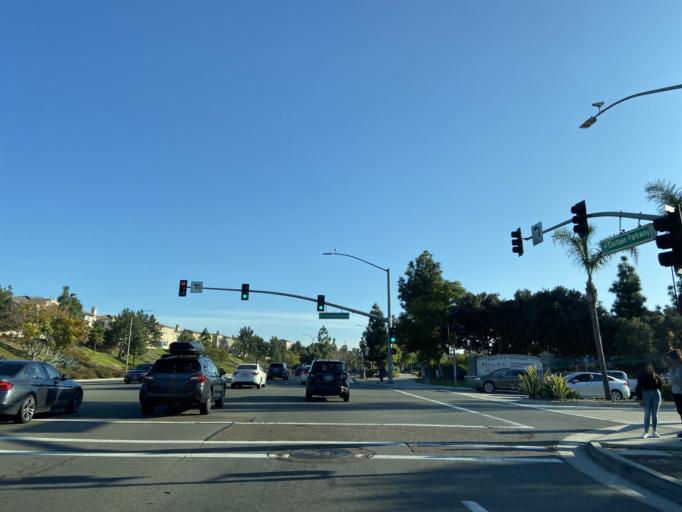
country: US
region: California
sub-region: San Diego County
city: Bonita
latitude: 32.6307
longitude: -116.9655
